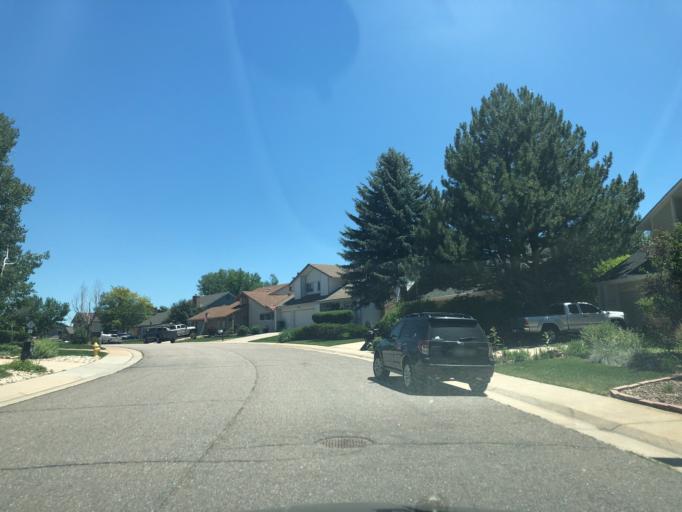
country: US
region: Colorado
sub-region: Arapahoe County
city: Dove Valley
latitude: 39.6155
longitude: -104.7790
